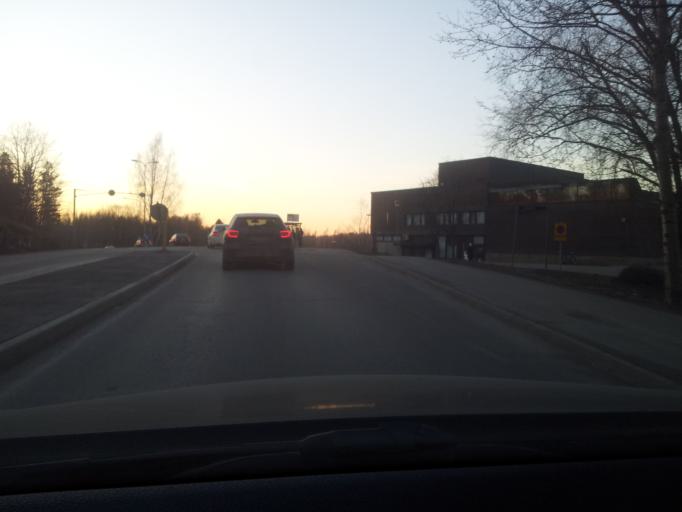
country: FI
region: Uusimaa
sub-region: Helsinki
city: Kilo
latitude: 60.2224
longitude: 24.8045
